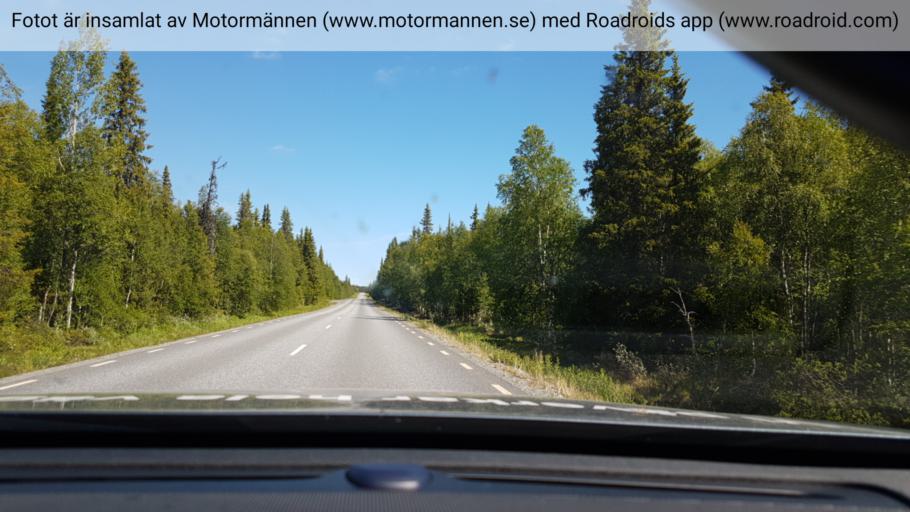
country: SE
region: Vaesterbotten
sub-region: Storumans Kommun
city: Storuman
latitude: 64.7038
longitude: 17.2071
